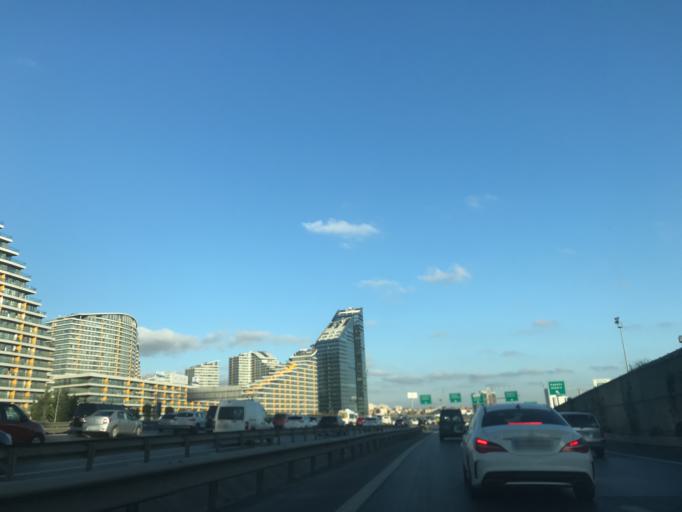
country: TR
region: Istanbul
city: Mahmutbey
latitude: 41.0635
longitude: 28.8365
